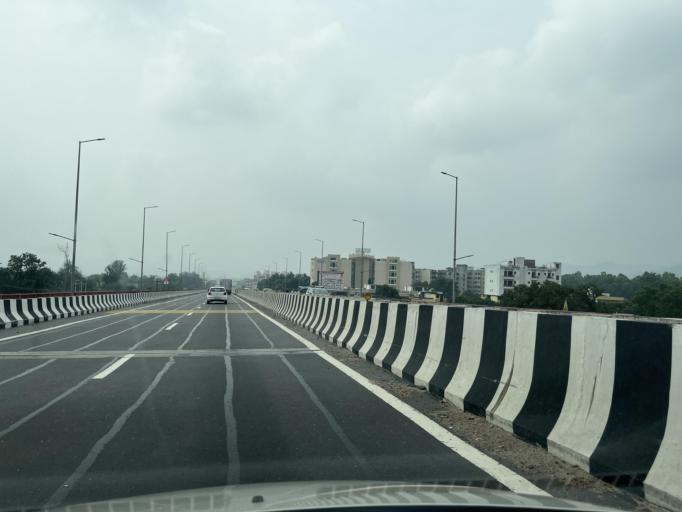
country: IN
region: Uttarakhand
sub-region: Dehradun
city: Raiwala
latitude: 30.0047
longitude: 78.1901
